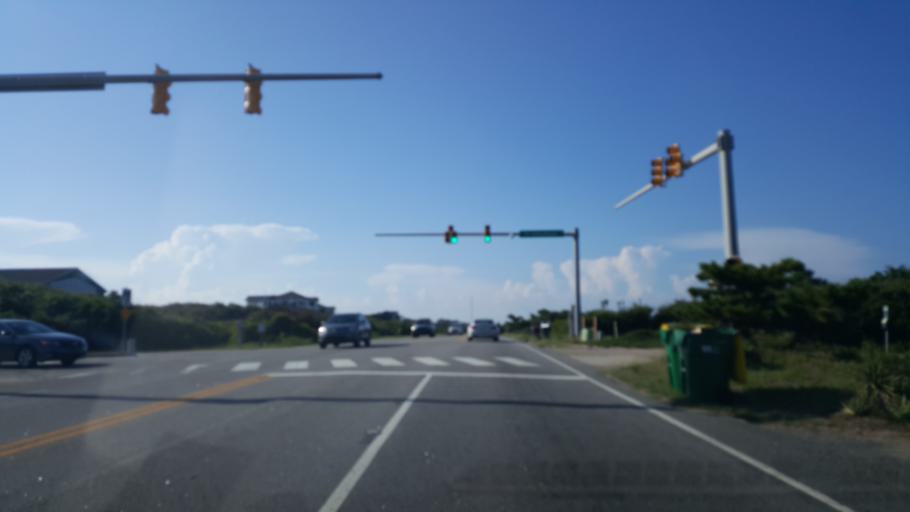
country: US
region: North Carolina
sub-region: Dare County
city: Southern Shores
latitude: 36.1143
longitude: -75.7200
